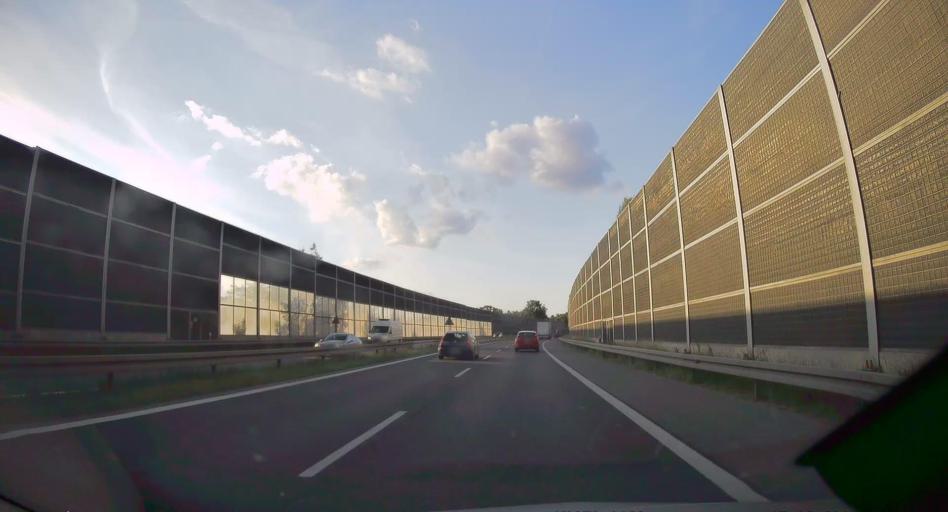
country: PL
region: Silesian Voivodeship
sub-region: Myslowice
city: Myslowice
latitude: 50.1867
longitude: 19.1667
